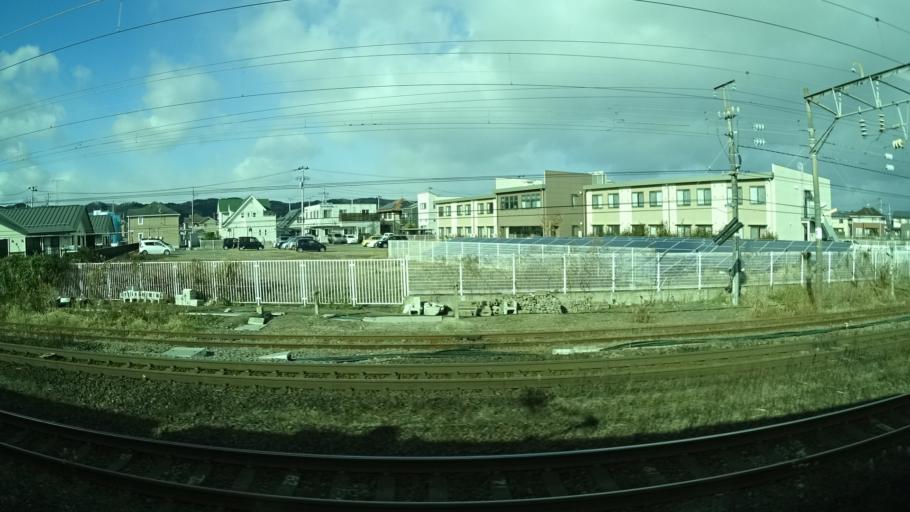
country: JP
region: Miyagi
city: Iwanuma
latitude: 38.1091
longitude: 140.8615
